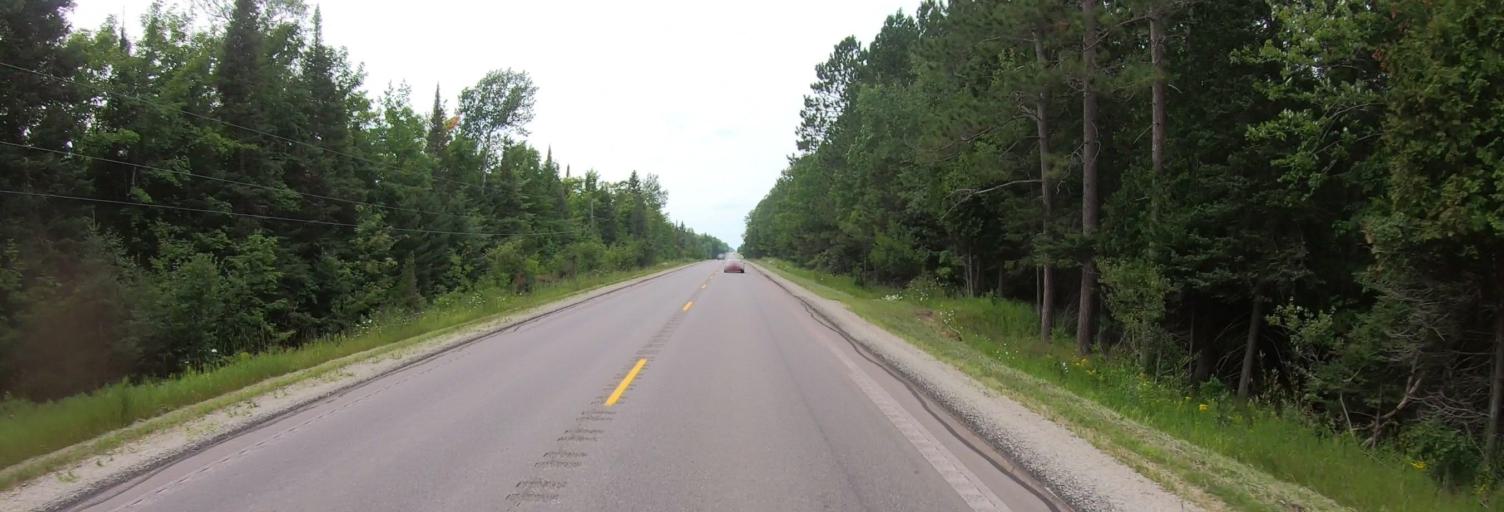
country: US
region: Michigan
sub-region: Marquette County
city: K. I. Sawyer Air Force Base
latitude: 46.3476
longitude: -87.1307
